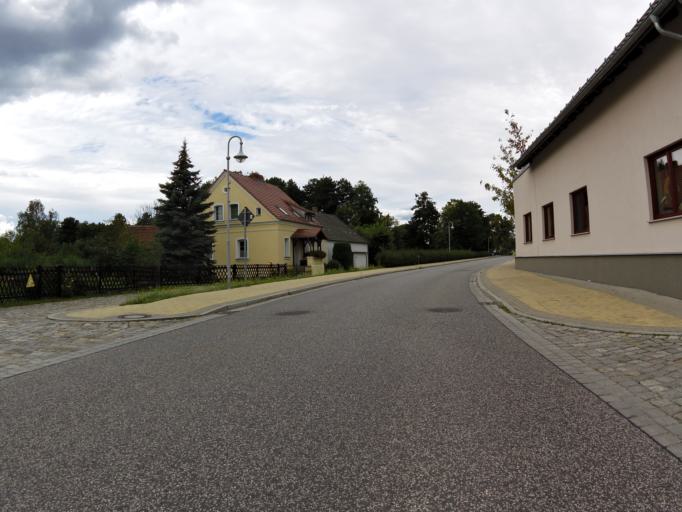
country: DE
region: Brandenburg
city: Wendisch Rietz
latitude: 52.2129
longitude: 14.0051
